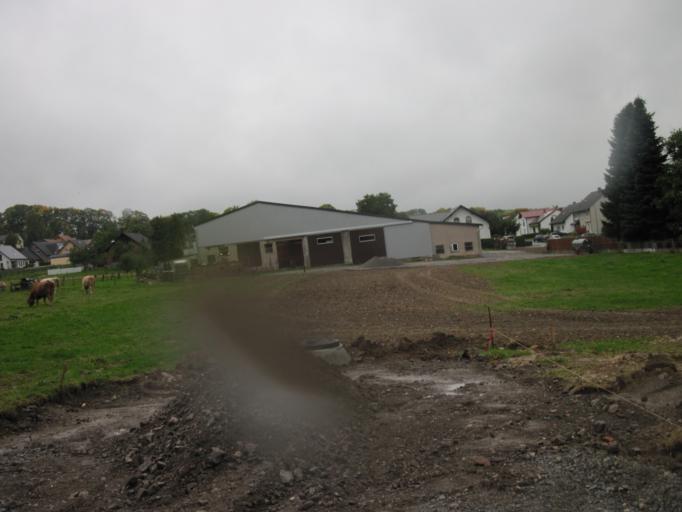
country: DE
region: North Rhine-Westphalia
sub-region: Regierungsbezirk Detmold
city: Wunnenberg
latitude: 51.5942
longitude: 8.7817
